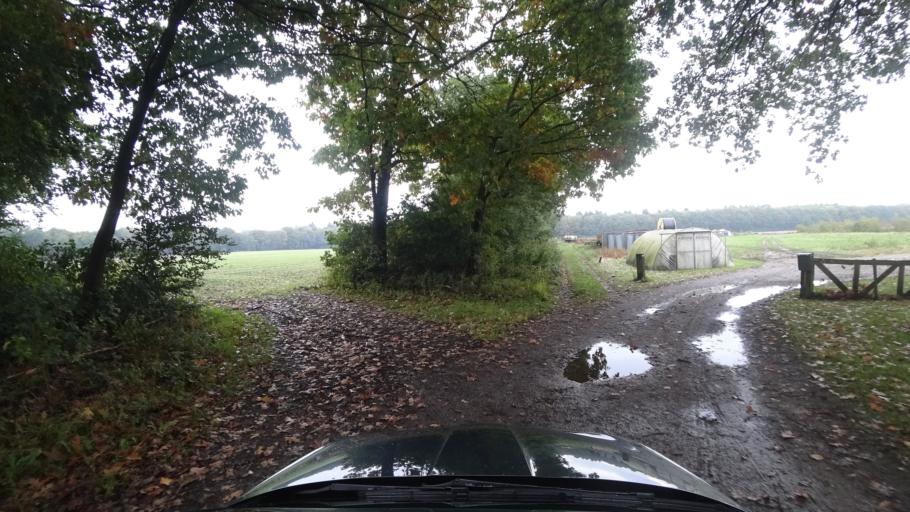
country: NL
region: Gelderland
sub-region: Gemeente Renkum
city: Wolfheze
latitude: 52.0037
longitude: 5.7747
